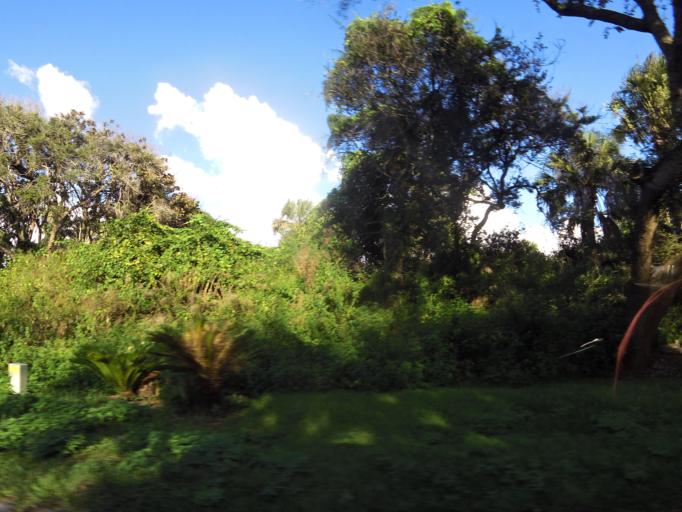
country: US
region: Florida
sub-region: Saint Johns County
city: Sawgrass
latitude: 30.1759
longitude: -81.3607
